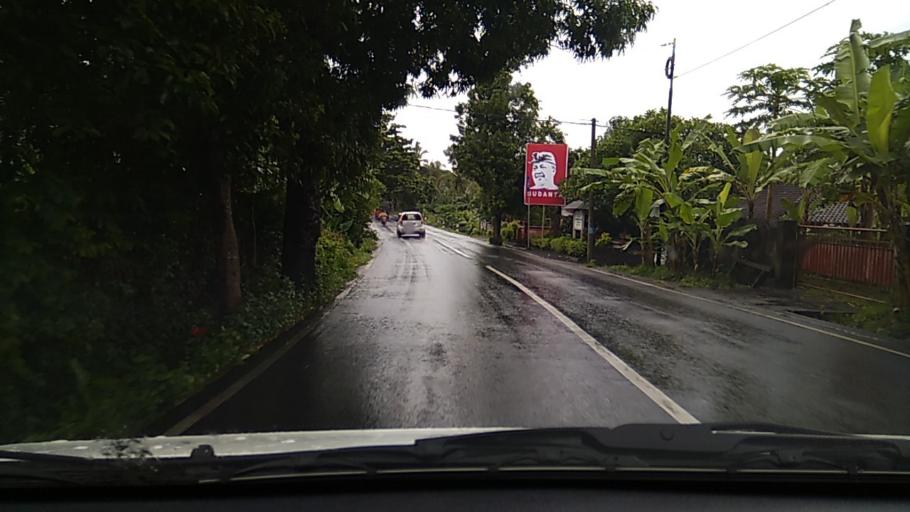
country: ID
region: Bali
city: Banjar Timbrah
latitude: -8.4840
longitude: 115.6047
